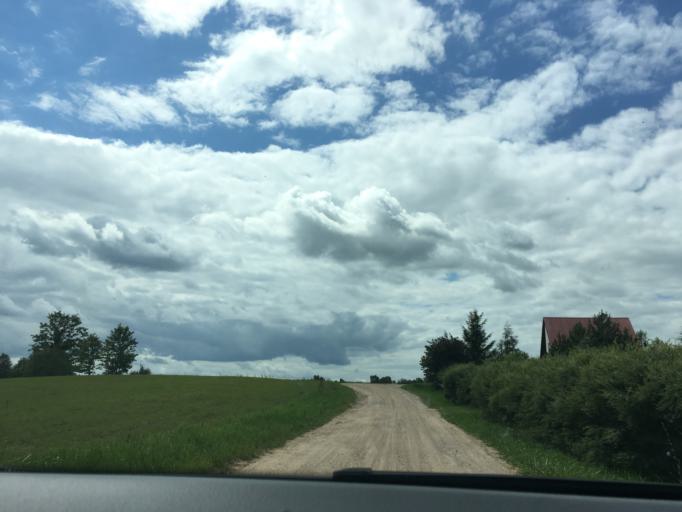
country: PL
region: Podlasie
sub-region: Powiat sejnenski
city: Krasnopol
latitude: 54.0992
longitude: 23.2716
